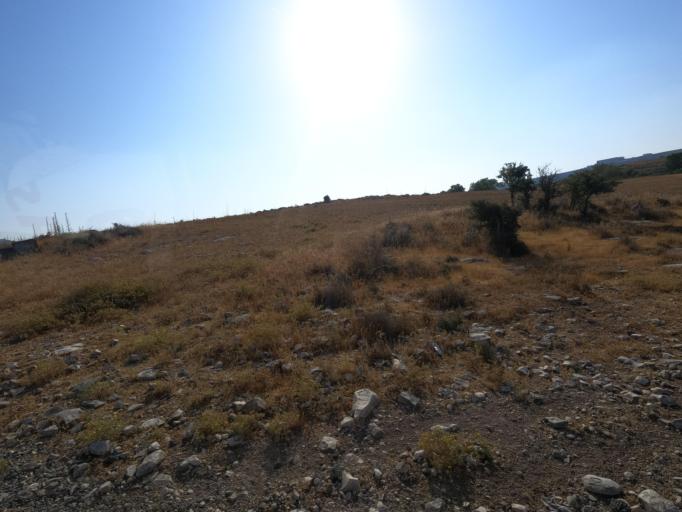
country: CY
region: Lefkosia
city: Lympia
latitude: 34.9915
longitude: 33.4497
